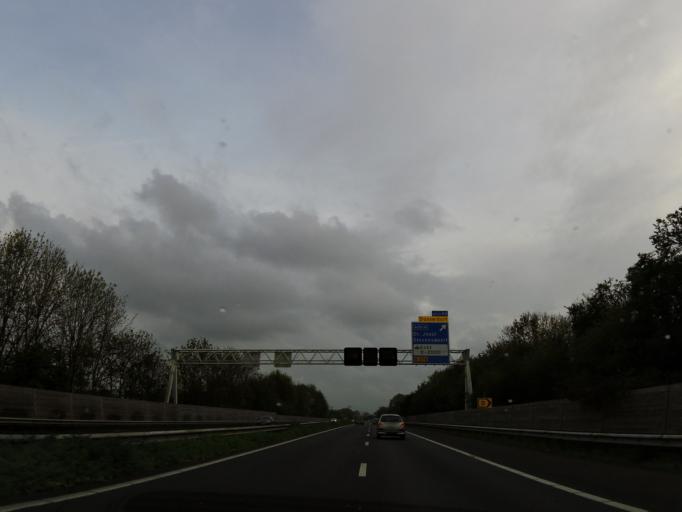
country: NL
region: Limburg
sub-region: Gemeente Maasgouw
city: Maasbracht
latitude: 51.1476
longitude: 5.8976
